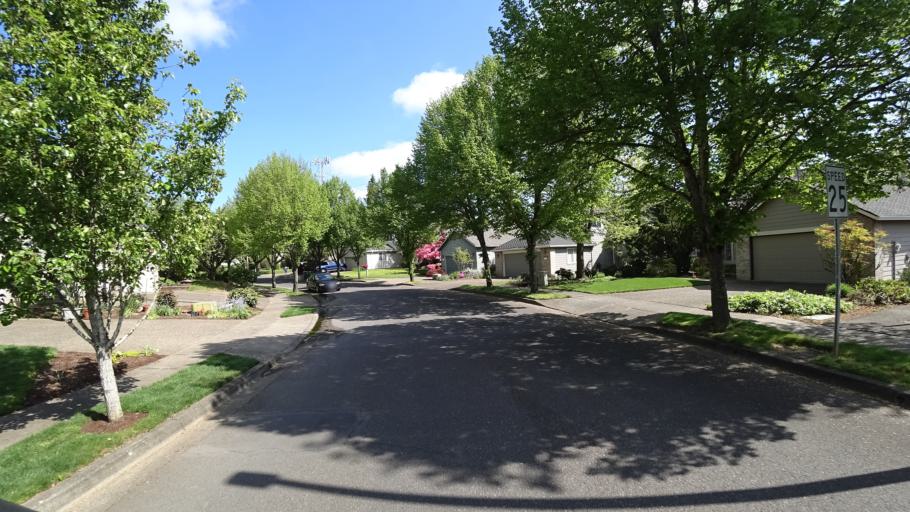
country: US
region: Oregon
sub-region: Washington County
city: King City
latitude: 45.4370
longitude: -122.8327
